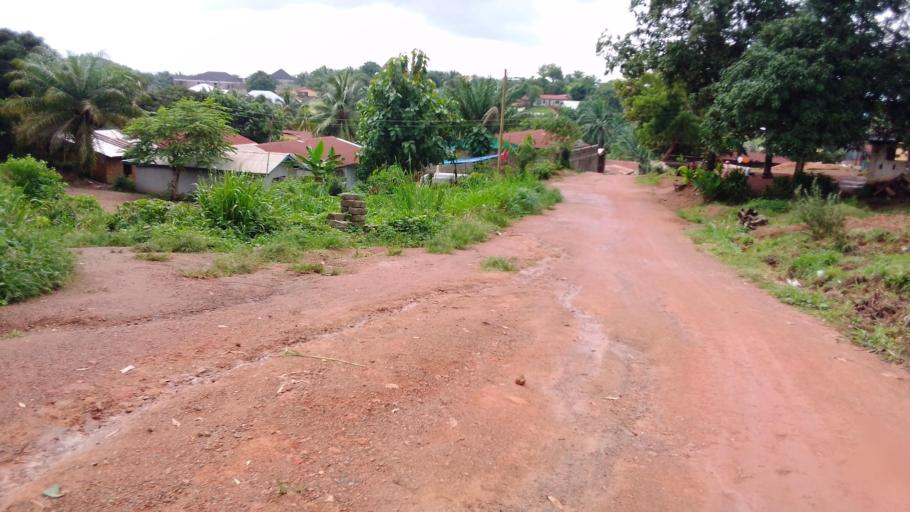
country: SL
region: Eastern Province
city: Kenema
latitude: 7.8726
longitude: -11.1766
